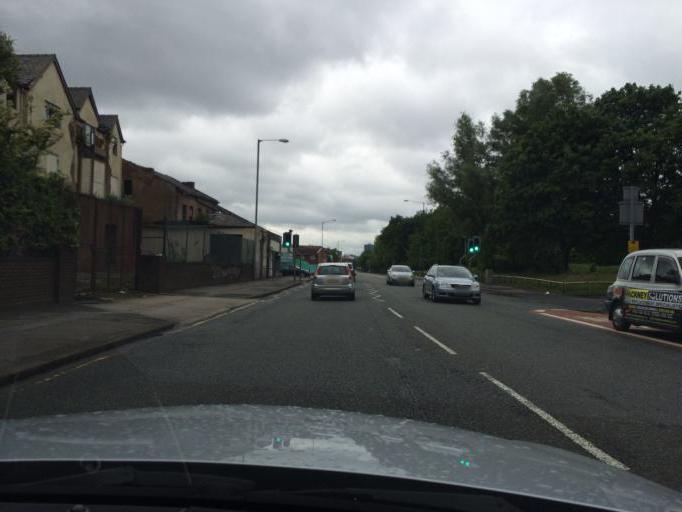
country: GB
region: England
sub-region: Manchester
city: Longsight
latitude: 53.4623
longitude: -2.2093
